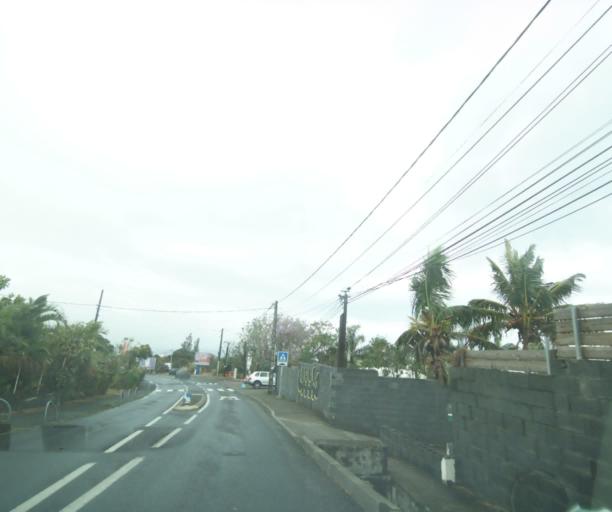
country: RE
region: Reunion
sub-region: Reunion
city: Saint-Paul
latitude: -21.0346
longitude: 55.2711
